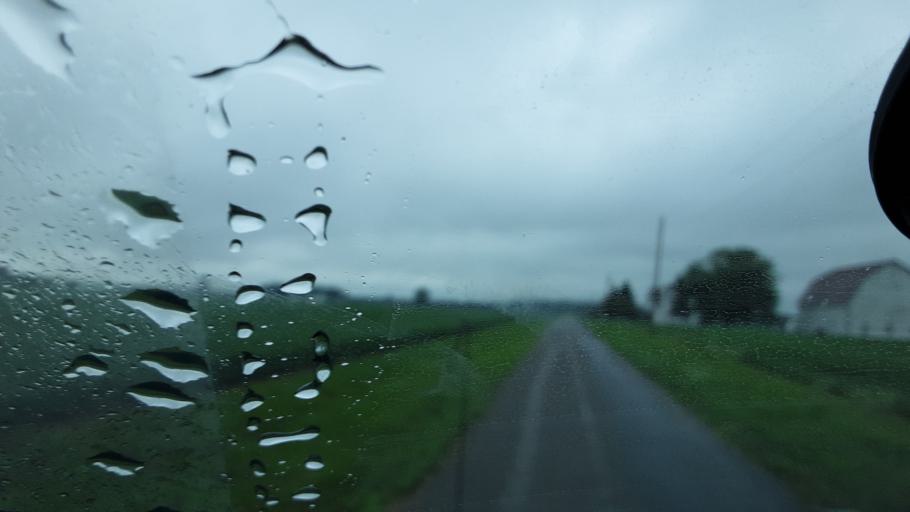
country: US
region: Ohio
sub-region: Mercer County
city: Rockford
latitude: 40.7498
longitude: -84.6529
